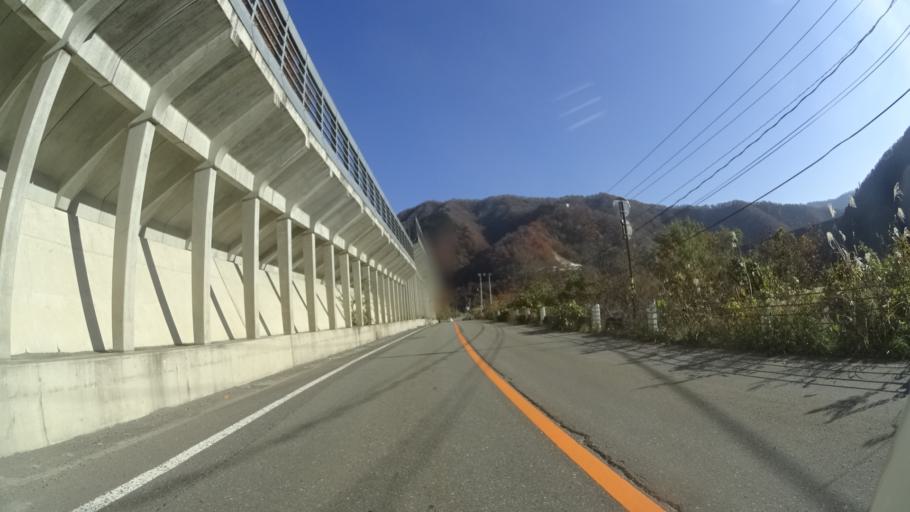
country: JP
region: Fukui
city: Ono
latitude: 35.8967
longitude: 136.6860
